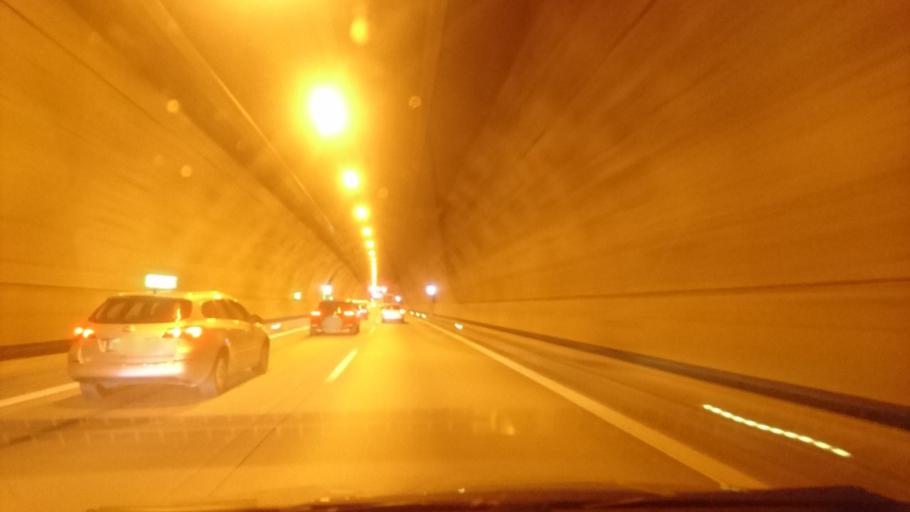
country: DE
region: Bavaria
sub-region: Upper Palatinate
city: Lappersdorf
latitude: 49.0320
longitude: 12.0832
